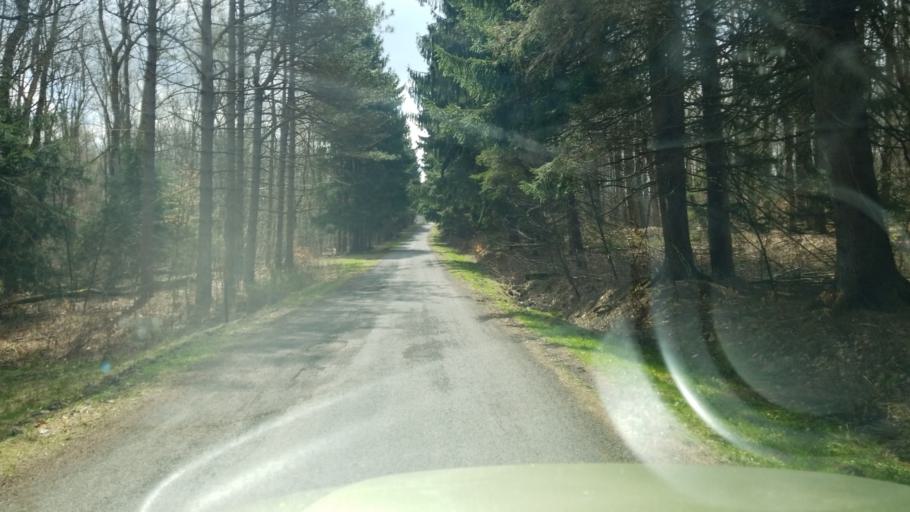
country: US
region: Pennsylvania
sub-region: Jefferson County
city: Brockway
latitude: 41.2825
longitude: -78.8714
